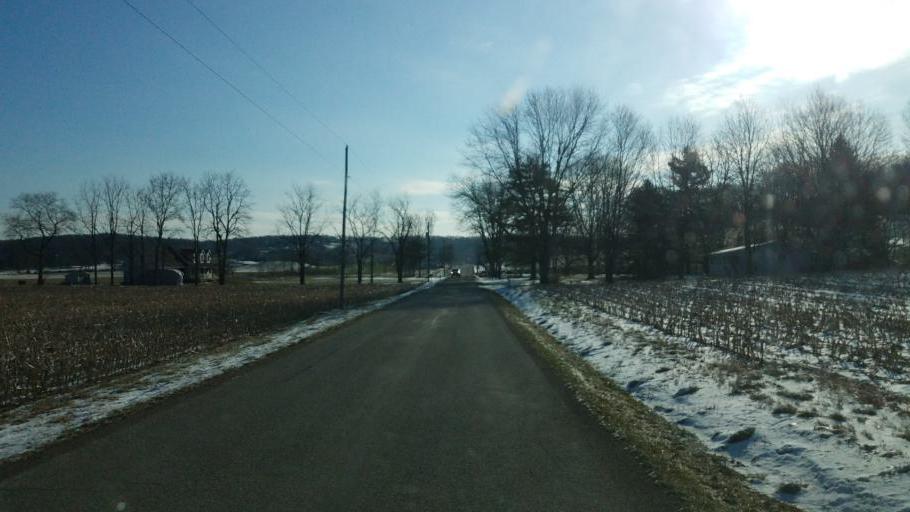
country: US
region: Ohio
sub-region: Sandusky County
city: Bellville
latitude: 40.6058
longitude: -82.5253
